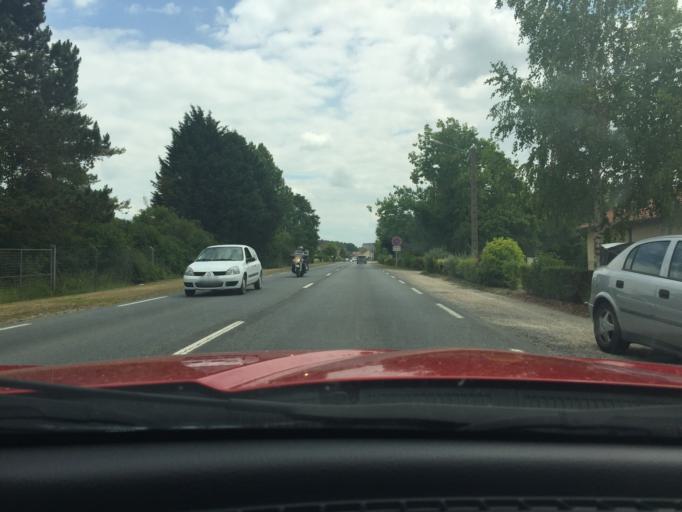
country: FR
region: Champagne-Ardenne
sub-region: Departement de la Marne
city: Cormicy
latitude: 49.4075
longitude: 3.8932
